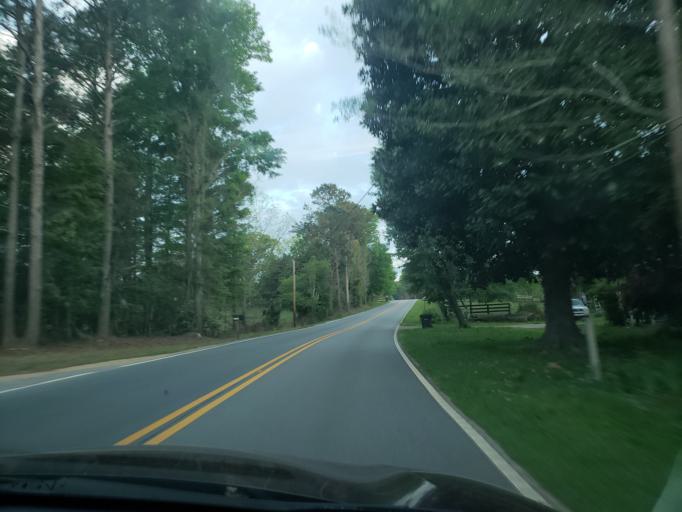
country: US
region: Alabama
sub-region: Tallapoosa County
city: Camp Hill
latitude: 32.6981
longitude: -85.7353
